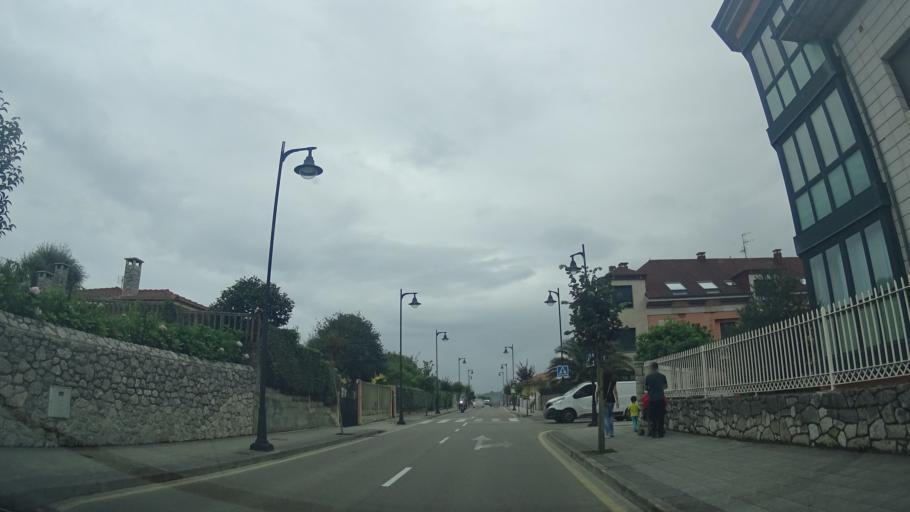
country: ES
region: Asturias
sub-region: Province of Asturias
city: Llanes
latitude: 43.4246
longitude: -4.7583
